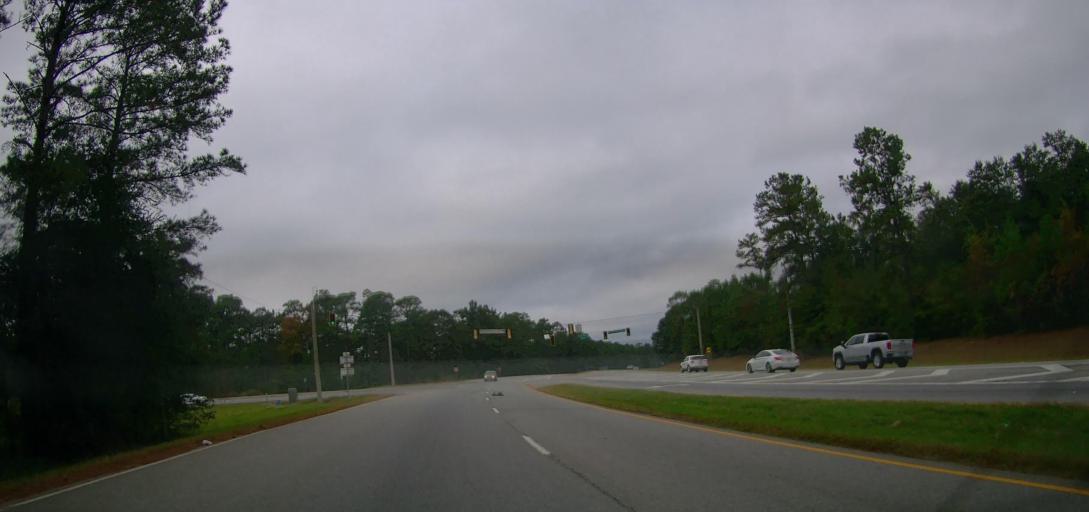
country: US
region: Georgia
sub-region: Thomas County
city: Thomasville
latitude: 30.8686
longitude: -84.0051
